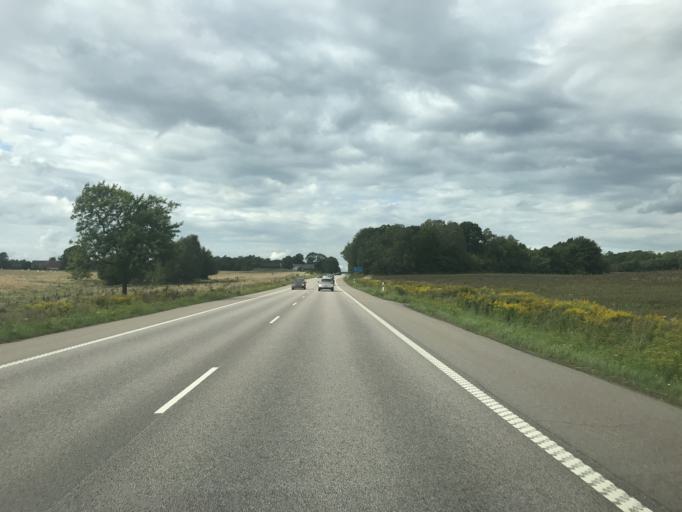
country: SE
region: Skane
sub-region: Hassleholms Kommun
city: Hassleholm
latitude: 56.1359
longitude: 13.8114
